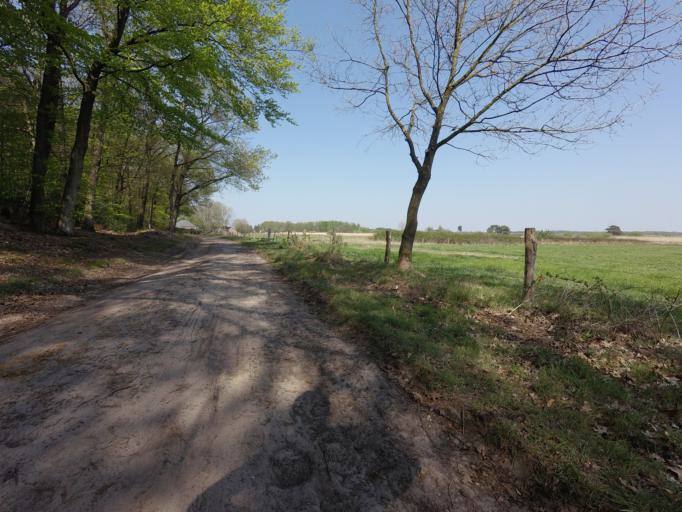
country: NL
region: North Brabant
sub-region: Gemeente Goirle
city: Goirle
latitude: 51.5022
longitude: 5.0164
